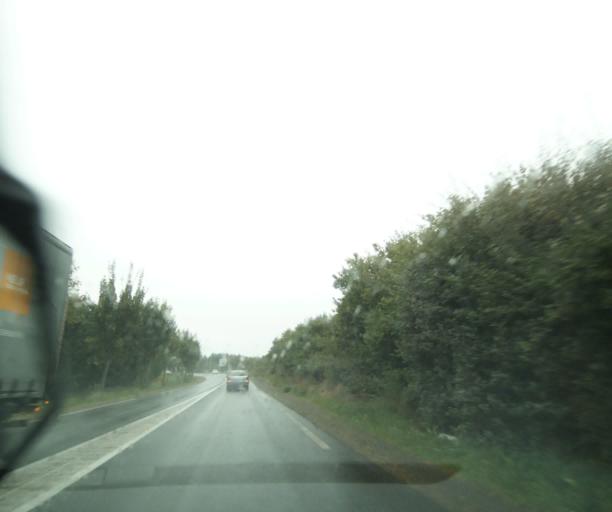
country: FR
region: Auvergne
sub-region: Departement du Puy-de-Dome
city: Blanzat
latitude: 45.8292
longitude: 3.0852
